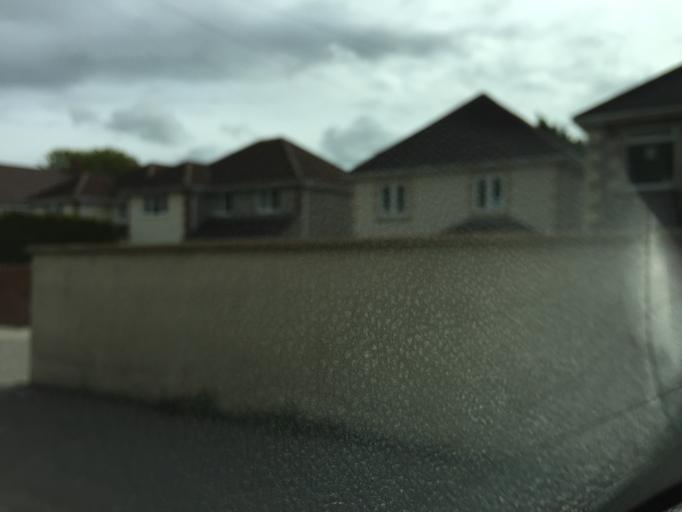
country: GB
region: England
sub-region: Bath and North East Somerset
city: Radstock
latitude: 51.2828
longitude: -2.4696
